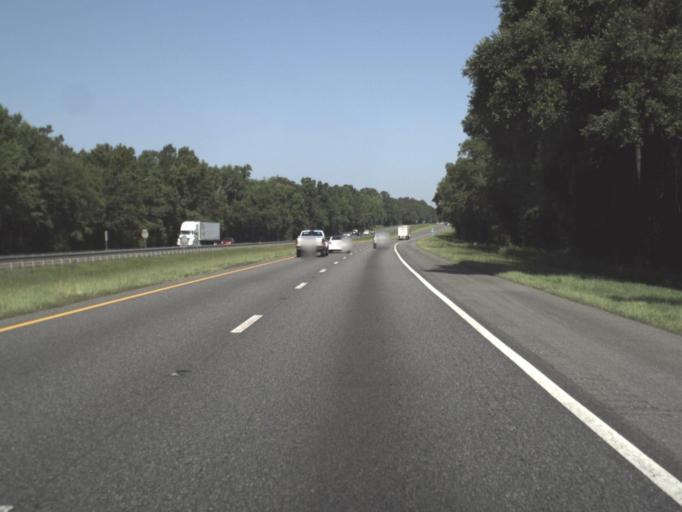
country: US
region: Florida
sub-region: Suwannee County
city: Wellborn
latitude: 30.2761
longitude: -82.8061
